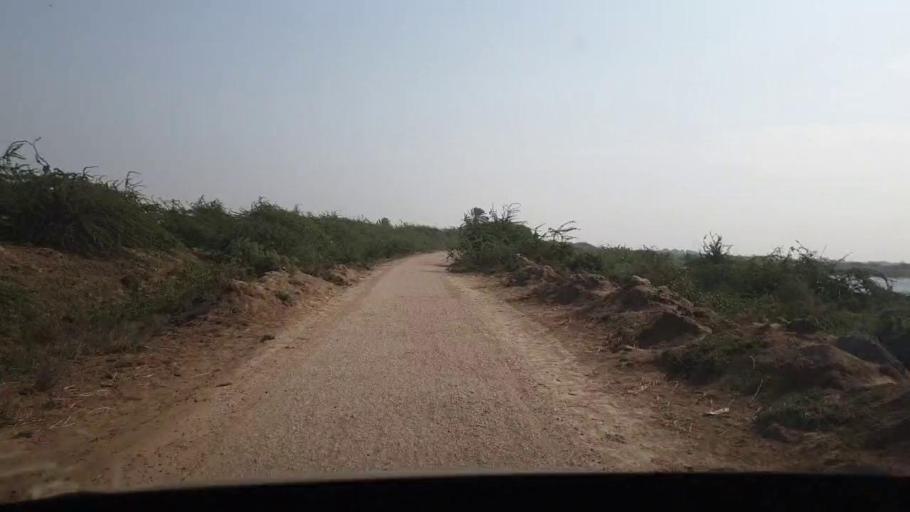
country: PK
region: Sindh
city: Chuhar Jamali
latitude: 24.2526
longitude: 67.9878
